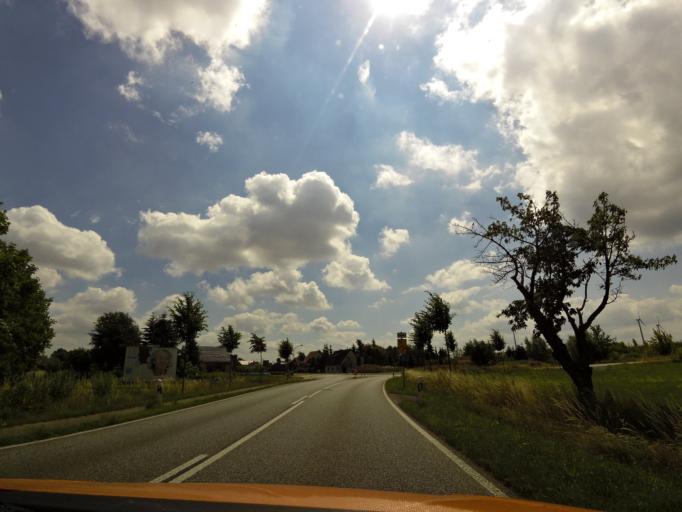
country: DE
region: Brandenburg
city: Wusterhausen
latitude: 52.8667
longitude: 12.4846
